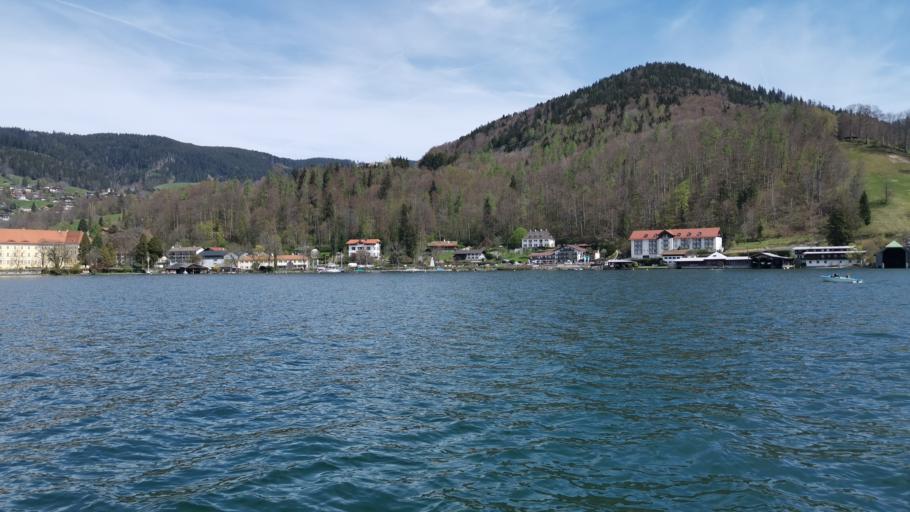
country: DE
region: Bavaria
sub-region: Upper Bavaria
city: Tegernsee
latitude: 47.7027
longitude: 11.7547
